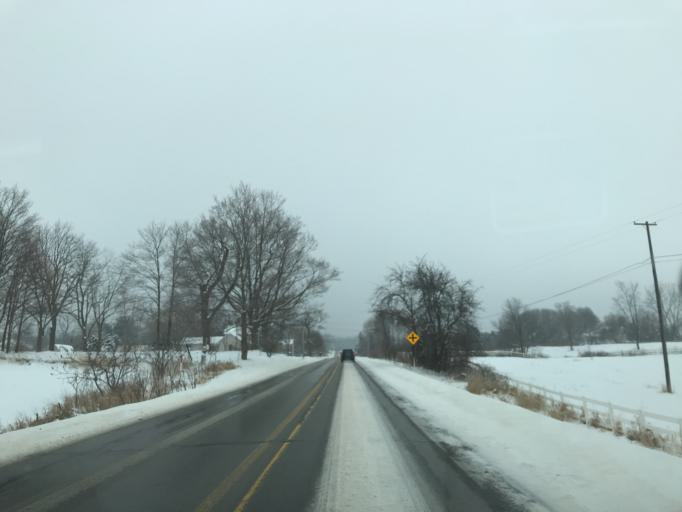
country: US
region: Michigan
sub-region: Oakland County
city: South Lyon
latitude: 42.3902
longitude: -83.6451
